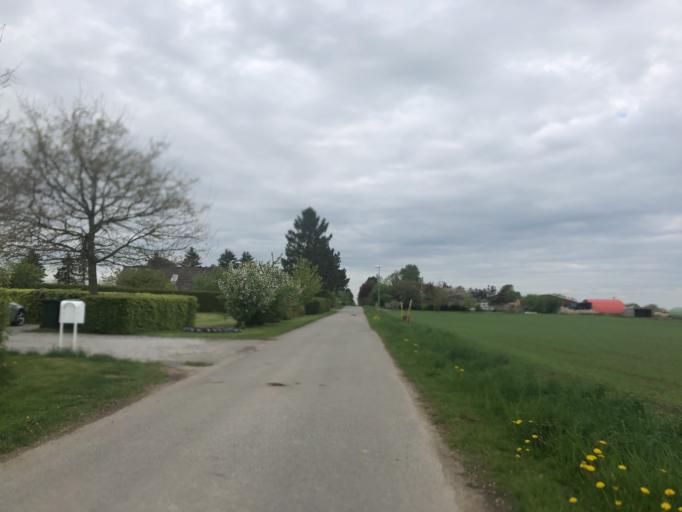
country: DK
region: Zealand
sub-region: Koge Kommune
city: Ejby
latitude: 55.4514
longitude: 12.0990
